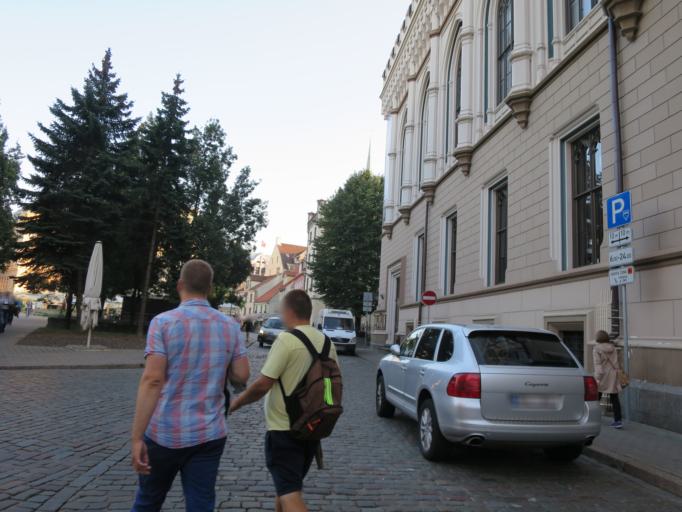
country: LV
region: Riga
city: Riga
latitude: 56.9500
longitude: 24.1083
